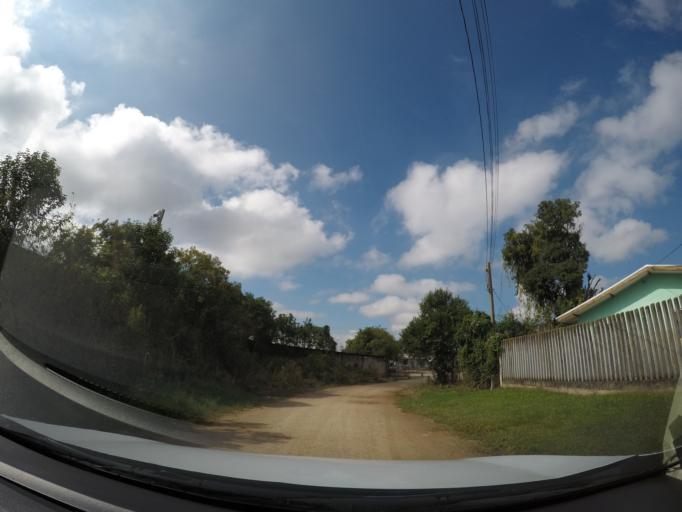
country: BR
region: Parana
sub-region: Sao Jose Dos Pinhais
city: Sao Jose dos Pinhais
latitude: -25.4953
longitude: -49.2198
